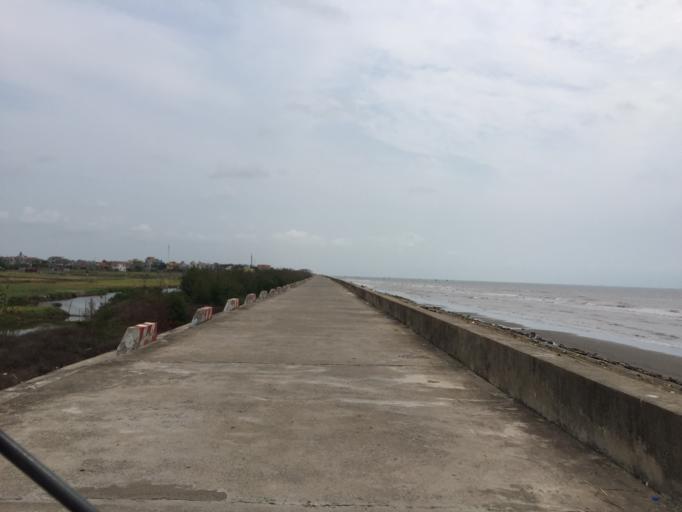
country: VN
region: Ninh Binh
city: Thi Tran Phat Diem
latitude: 20.0154
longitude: 106.2103
